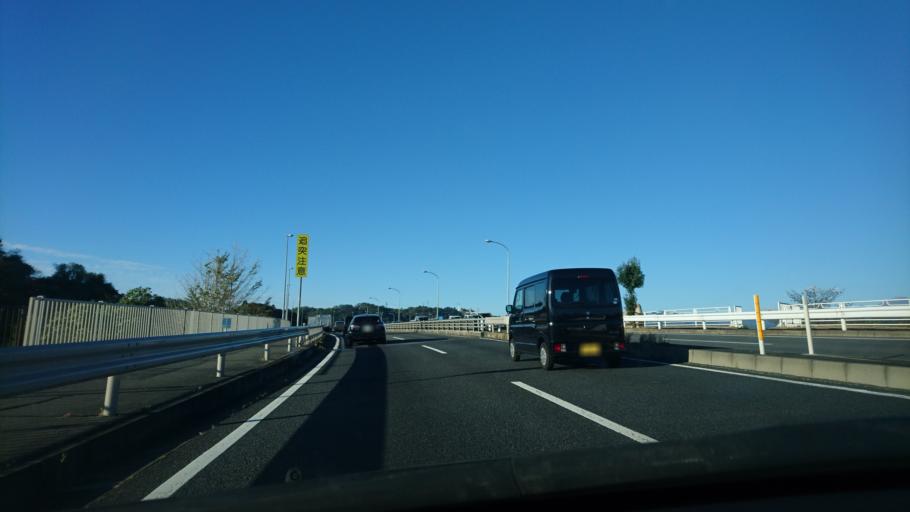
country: JP
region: Gunma
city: Annaka
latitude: 36.3353
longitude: 138.9378
